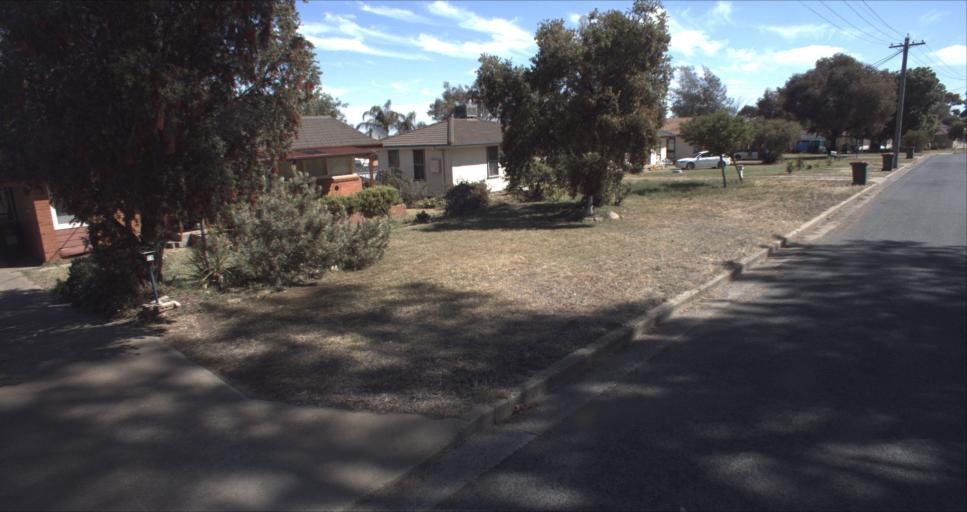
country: AU
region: New South Wales
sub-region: Leeton
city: Leeton
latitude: -34.5517
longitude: 146.3774
